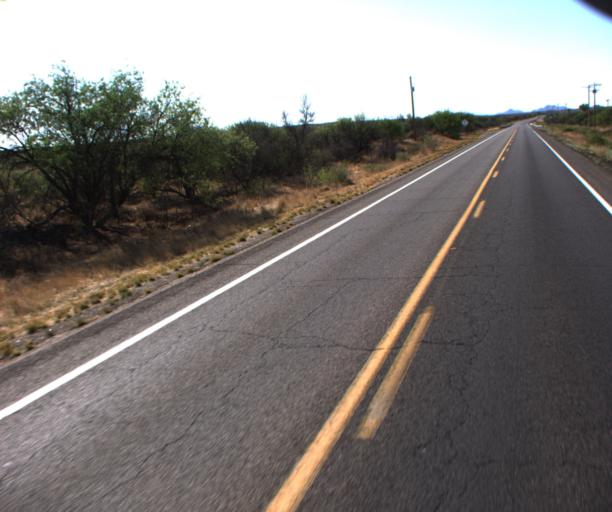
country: US
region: Arizona
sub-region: Cochise County
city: Saint David
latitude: 31.8646
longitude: -110.2061
